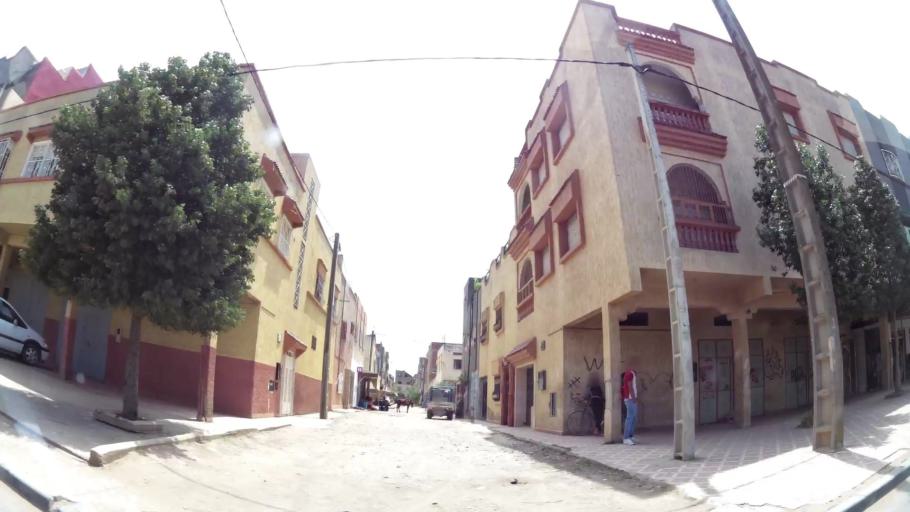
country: MA
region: Rabat-Sale-Zemmour-Zaer
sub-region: Khemisset
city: Khemisset
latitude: 33.8211
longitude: -6.0779
